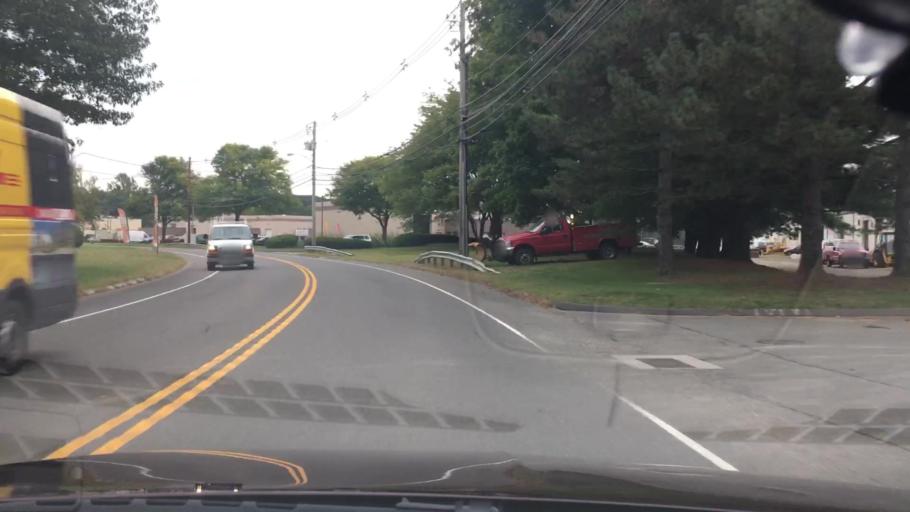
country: US
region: Connecticut
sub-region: New Haven County
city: Wallingford
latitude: 41.4792
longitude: -72.8197
